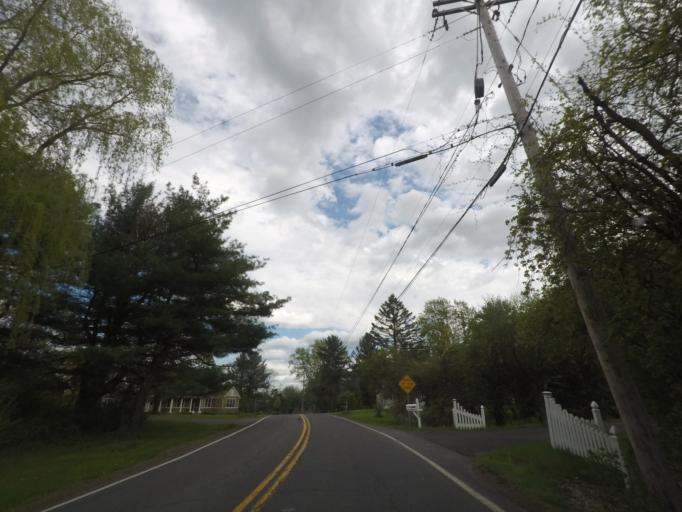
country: US
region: New York
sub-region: Albany County
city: Voorheesville
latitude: 42.6686
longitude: -73.9108
